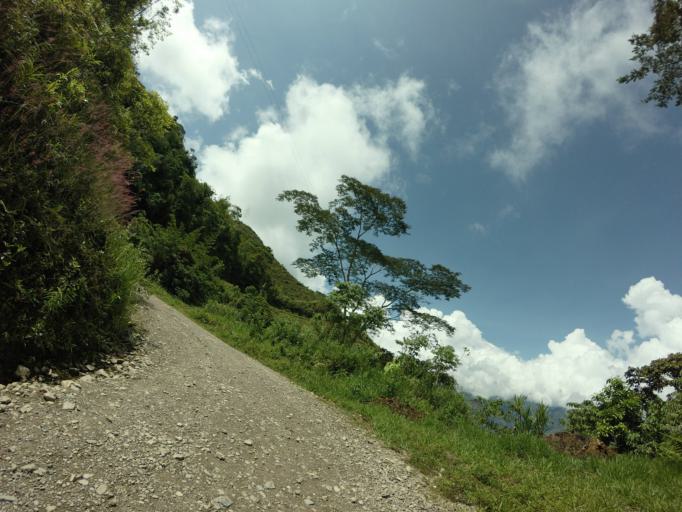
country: CO
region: Antioquia
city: Narino
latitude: 5.5125
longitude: -75.1740
